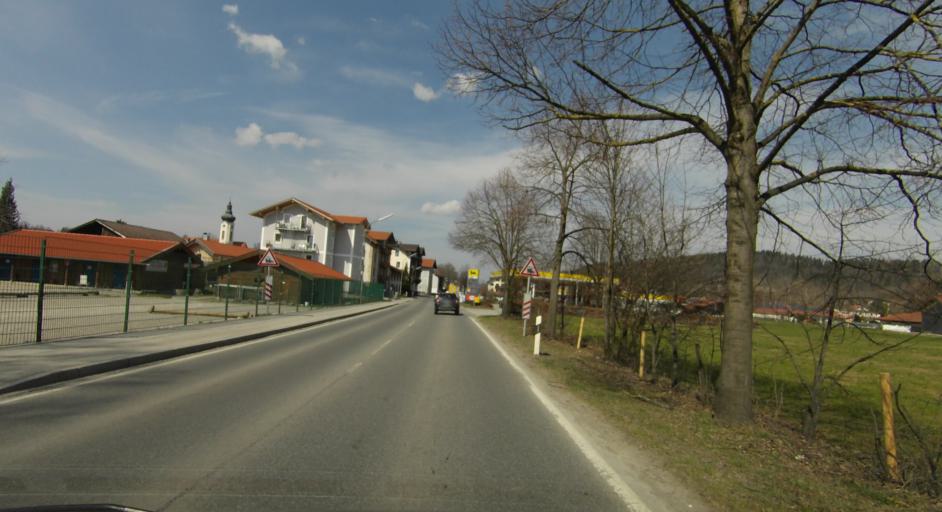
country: DE
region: Bavaria
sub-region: Upper Bavaria
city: Hausham
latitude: 47.7457
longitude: 11.8449
